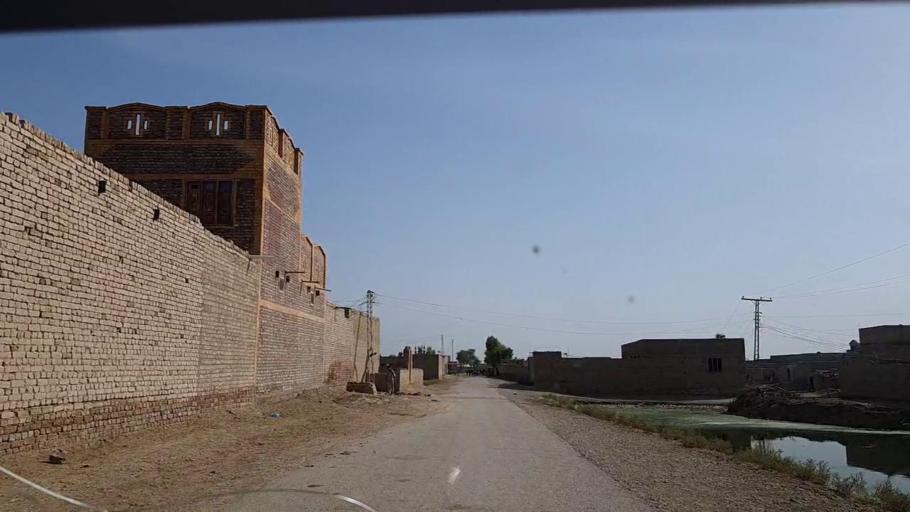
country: PK
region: Sindh
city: Phulji
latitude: 26.9927
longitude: 67.6645
